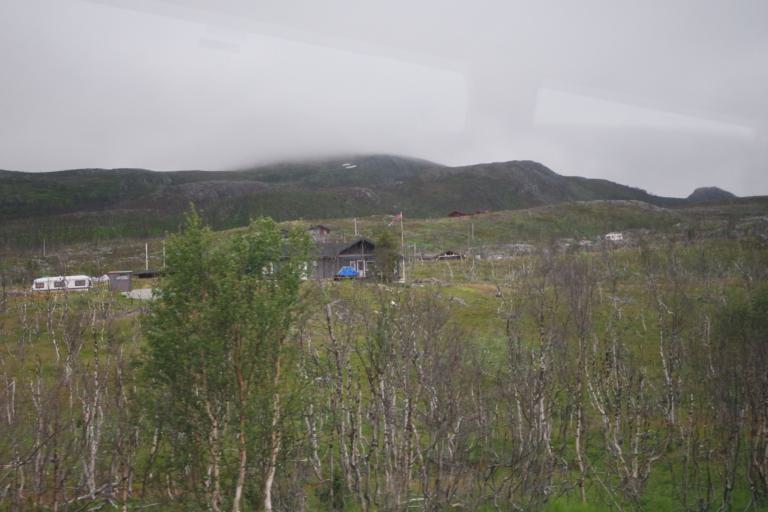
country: NO
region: Finnmark Fylke
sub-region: Kvalsund
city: Kvalsund
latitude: 70.3466
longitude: 24.3451
